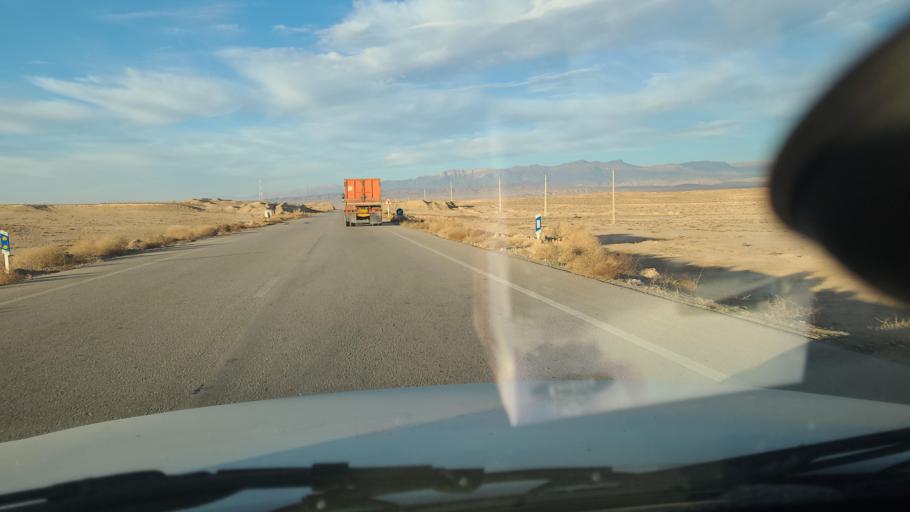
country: IR
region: Razavi Khorasan
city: Neqab
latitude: 36.7646
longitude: 57.5875
